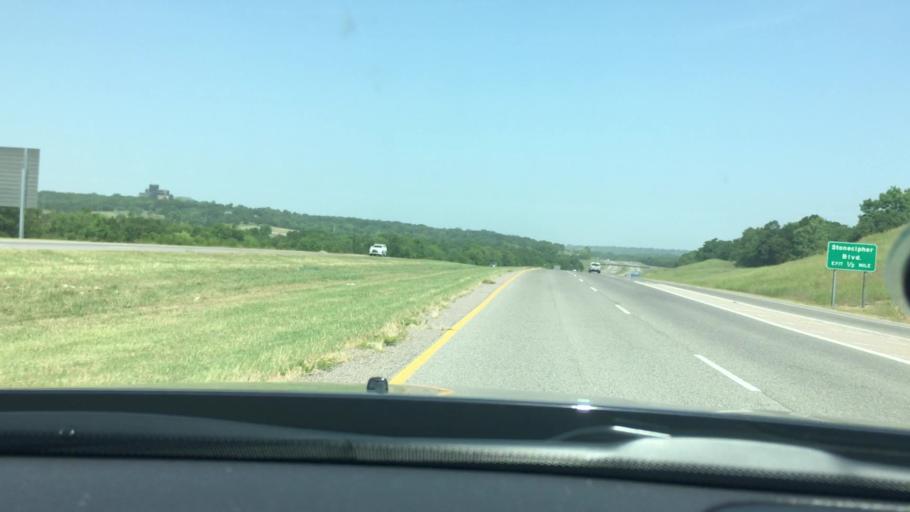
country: US
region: Oklahoma
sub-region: Pontotoc County
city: Ada
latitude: 34.7296
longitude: -96.6382
